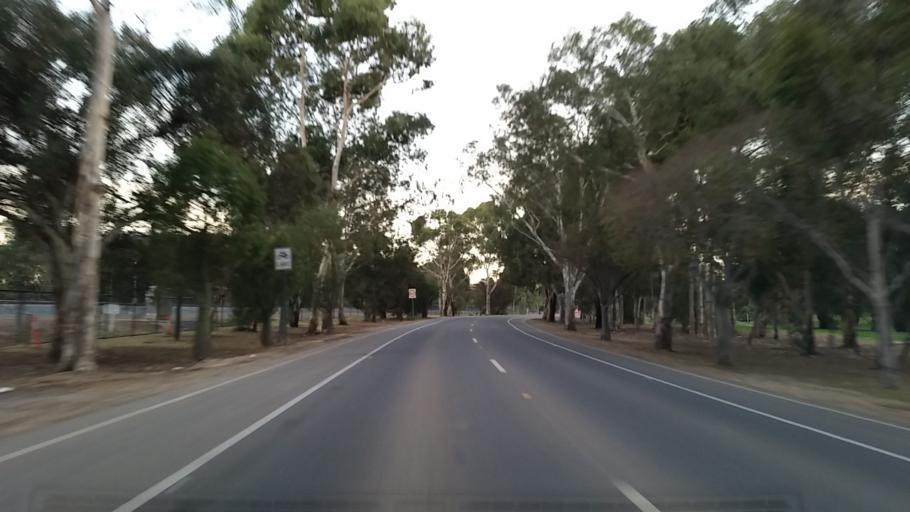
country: AU
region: South Australia
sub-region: Adelaide
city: North Adelaide
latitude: -34.9098
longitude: 138.5814
